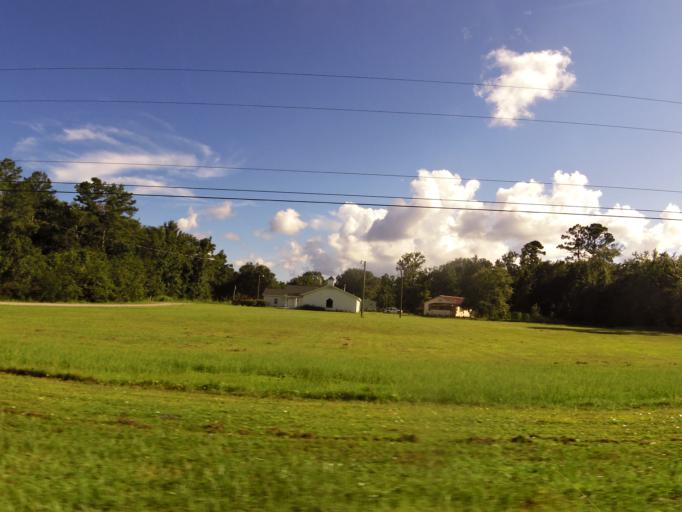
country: US
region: Georgia
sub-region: Camden County
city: Woodbine
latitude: 31.1065
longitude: -81.6489
